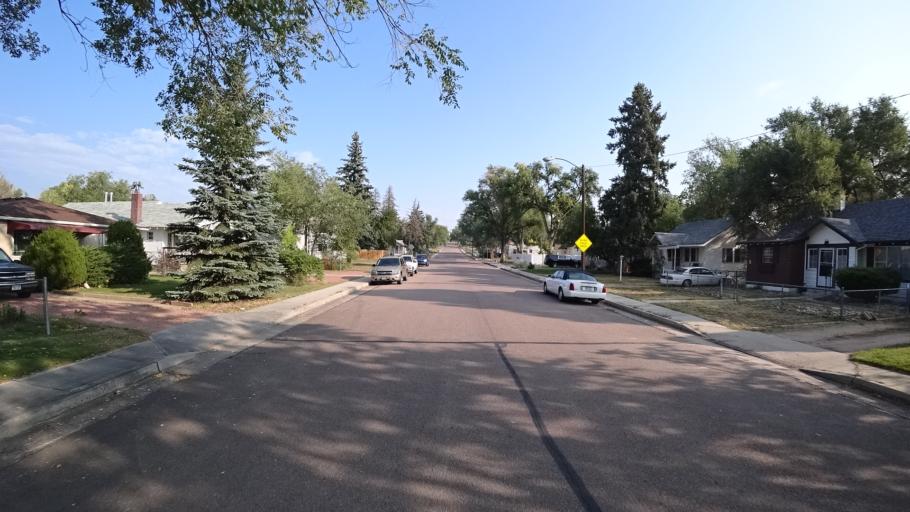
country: US
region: Colorado
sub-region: El Paso County
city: Colorado Springs
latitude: 38.8402
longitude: -104.7915
